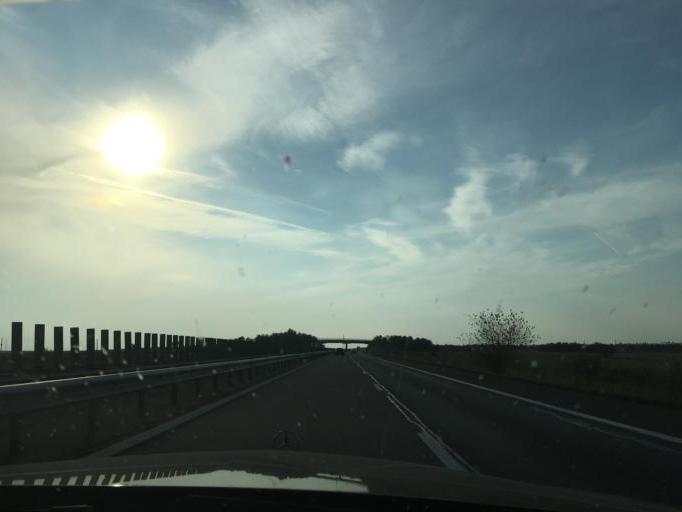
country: RO
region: Calarasi
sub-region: Comuna Lupsanu
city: Radu Voda
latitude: 44.4231
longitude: 26.9836
